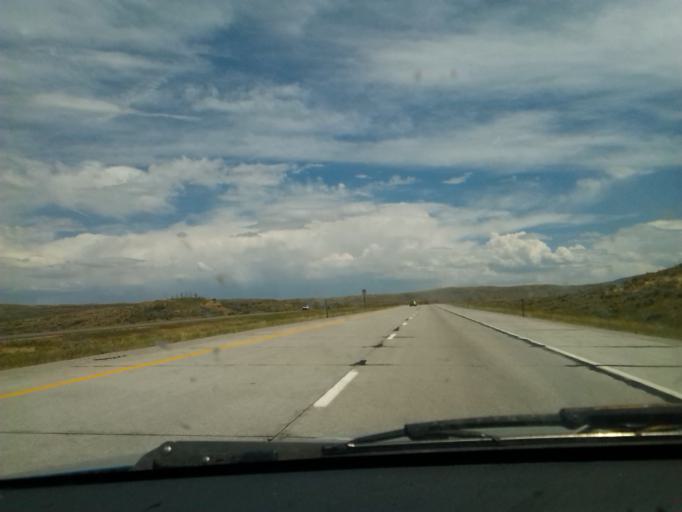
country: US
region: Wyoming
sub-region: Carbon County
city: Saratoga
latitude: 41.7309
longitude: -106.7062
